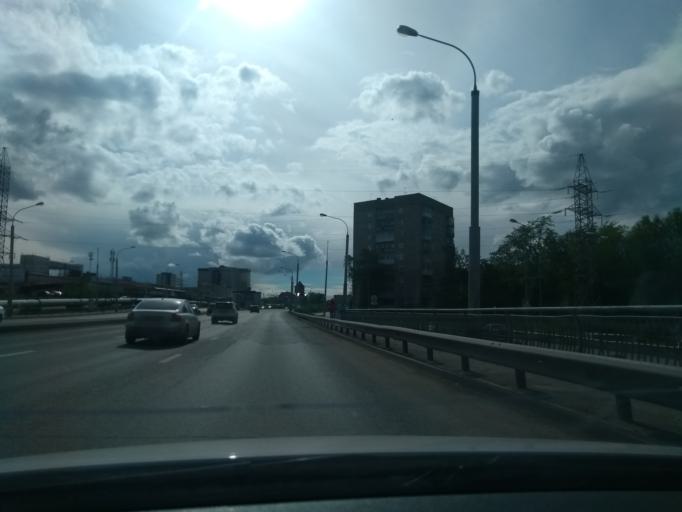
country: RU
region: Perm
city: Perm
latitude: 57.9863
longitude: 56.2721
